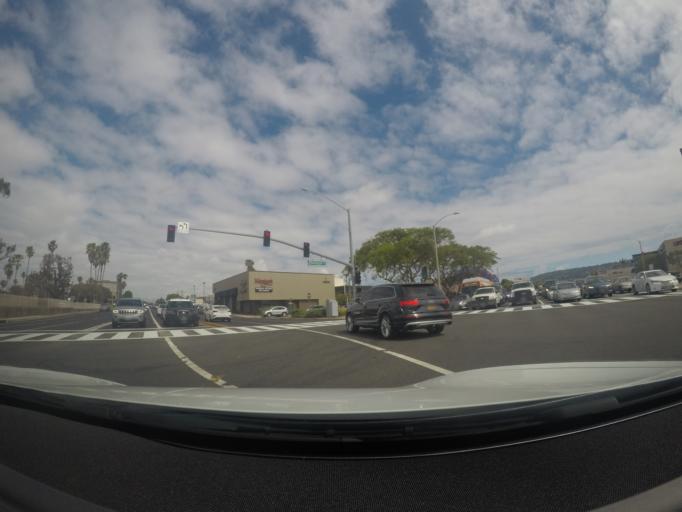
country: US
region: California
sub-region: Los Angeles County
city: Torrance
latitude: 33.8256
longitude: -118.3514
